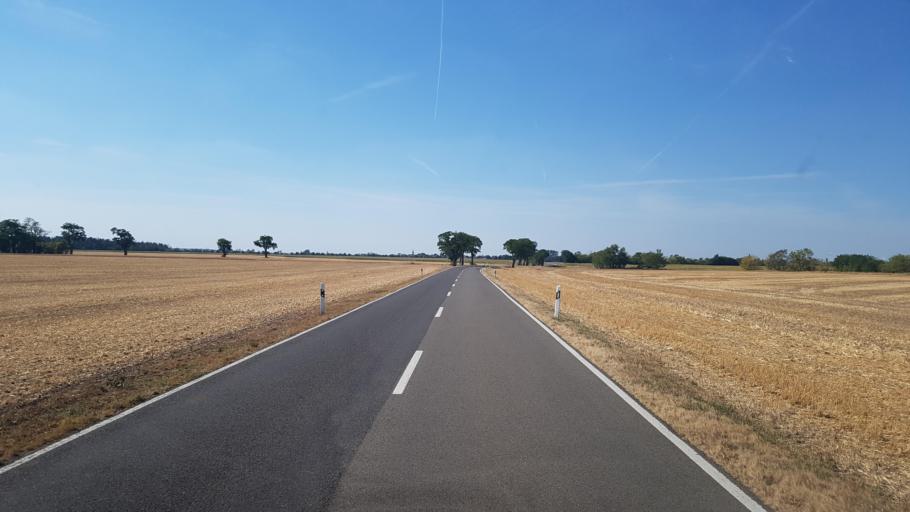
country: DE
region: Saxony
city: Strehla
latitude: 51.3900
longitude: 13.2745
